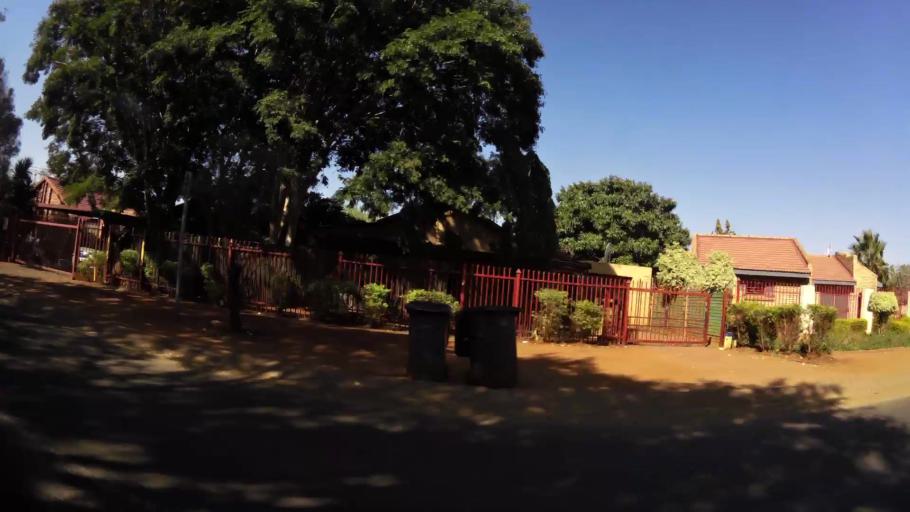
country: ZA
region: Gauteng
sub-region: City of Tshwane Metropolitan Municipality
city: Pretoria
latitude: -25.6576
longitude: 28.2559
